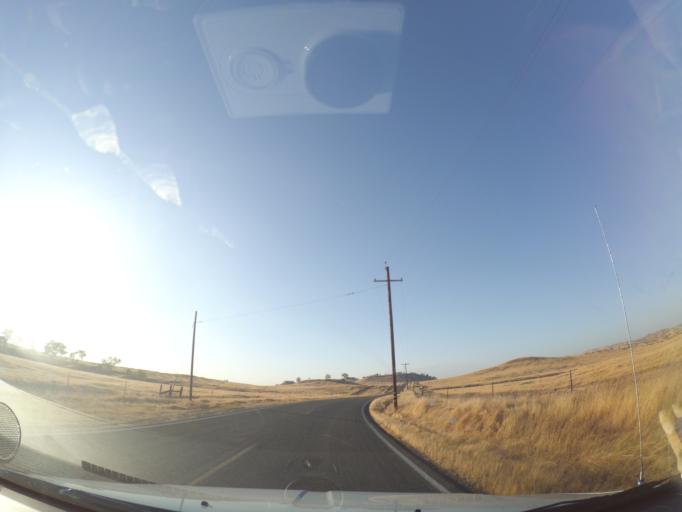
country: US
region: California
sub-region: Merced County
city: Planada
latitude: 37.4968
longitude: -120.3110
